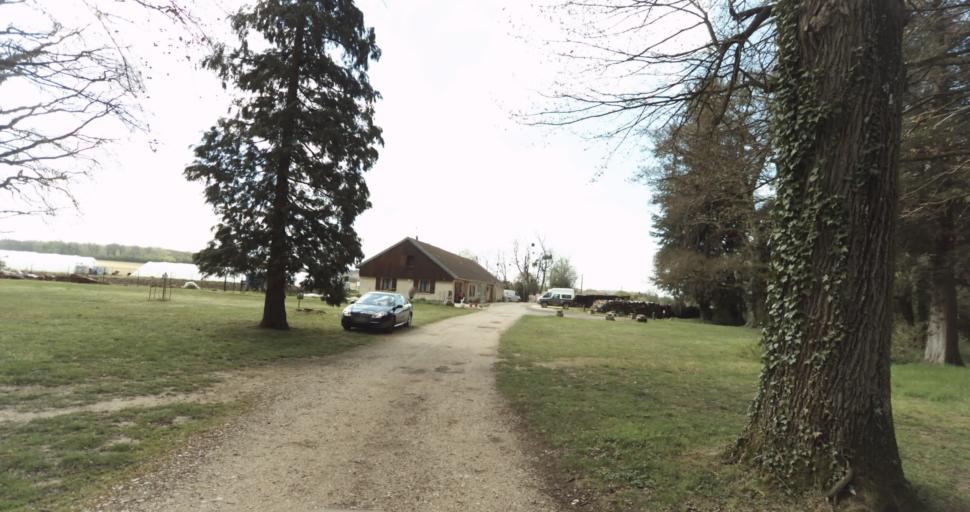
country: FR
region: Bourgogne
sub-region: Departement de la Cote-d'Or
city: Auxonne
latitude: 47.2027
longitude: 5.4294
